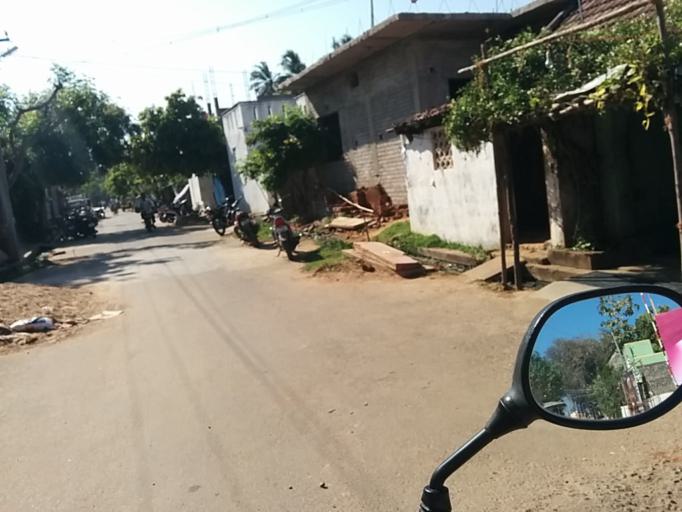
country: IN
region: Pondicherry
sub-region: Puducherry
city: Puducherry
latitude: 11.9619
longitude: 79.8284
